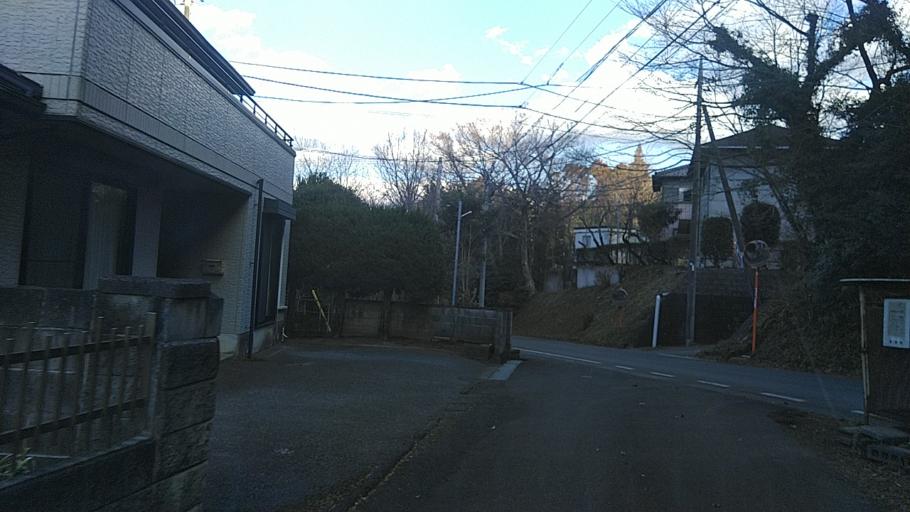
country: JP
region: Chiba
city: Kimitsu
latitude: 35.2856
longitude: 139.9748
